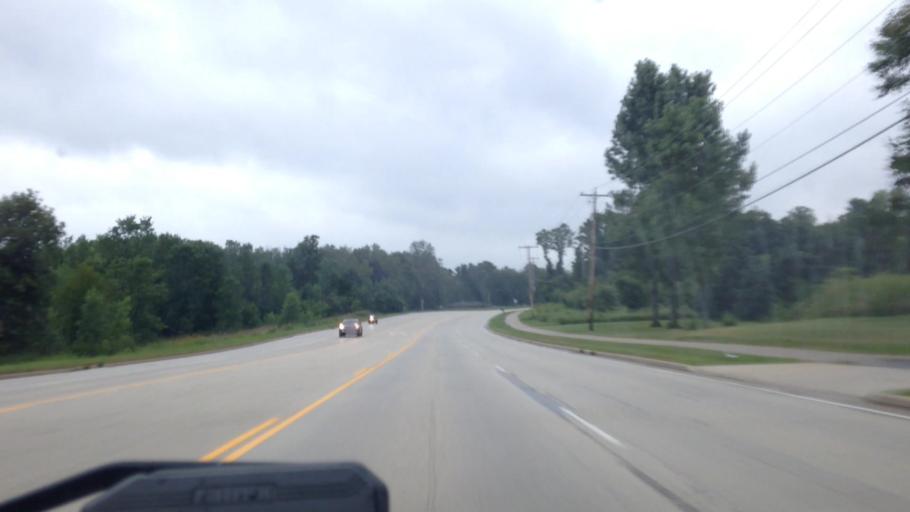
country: US
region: Wisconsin
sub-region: Waukesha County
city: Menomonee Falls
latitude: 43.1976
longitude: -88.1624
